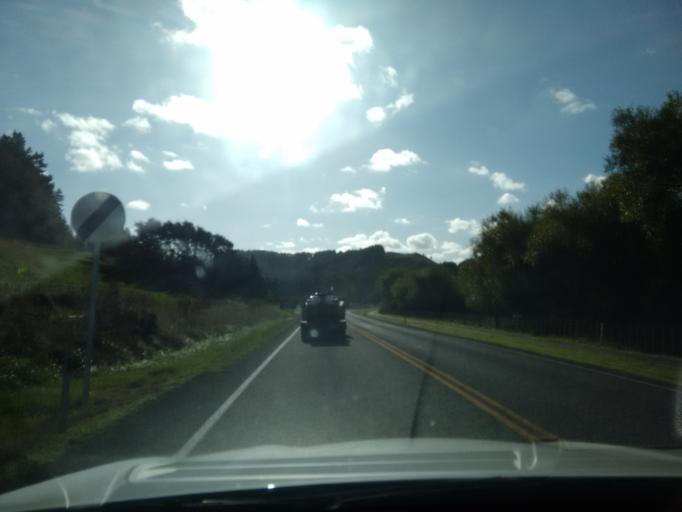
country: NZ
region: Manawatu-Wanganui
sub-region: Wanganui District
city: Wanganui
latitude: -39.8500
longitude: 174.9293
